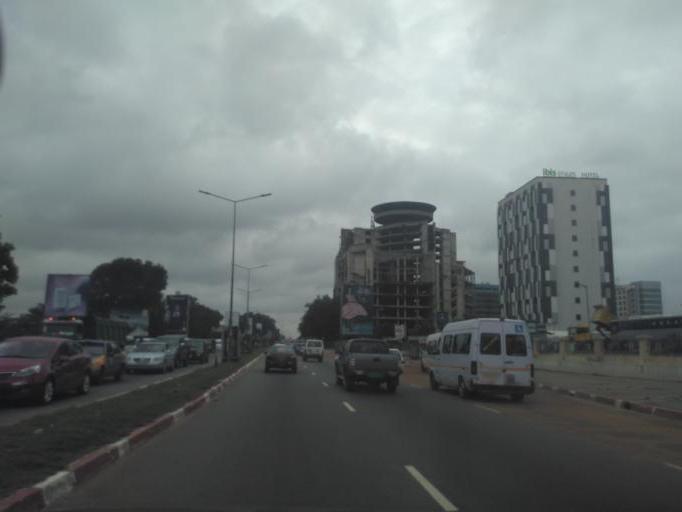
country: GH
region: Greater Accra
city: Accra
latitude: 5.6002
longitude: -0.1788
